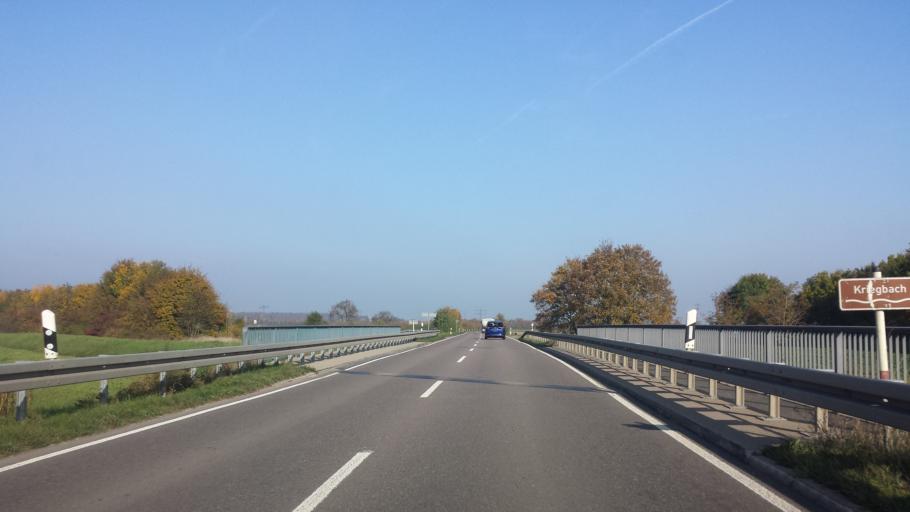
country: DE
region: Baden-Wuerttemberg
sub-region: Karlsruhe Region
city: Ubstadt-Weiher
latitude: 49.1915
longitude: 8.6298
